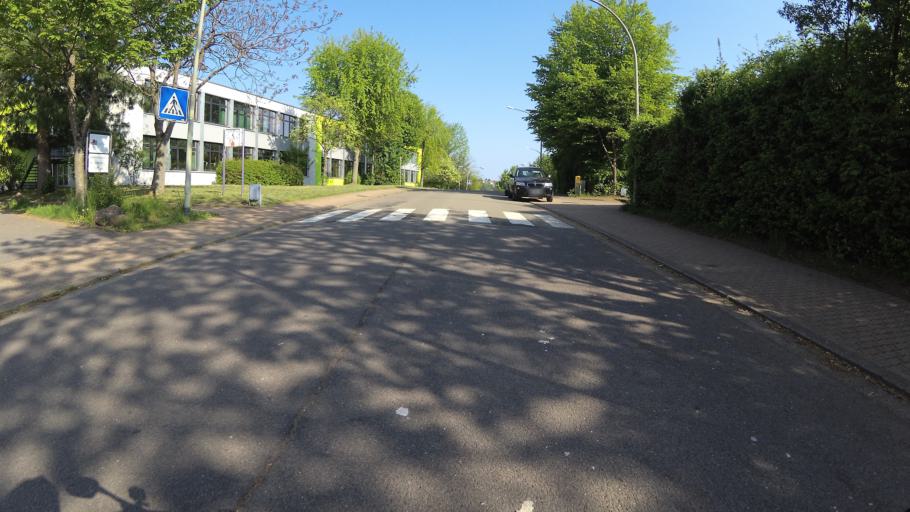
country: DE
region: Saarland
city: Illingen
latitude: 49.3678
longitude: 7.0419
